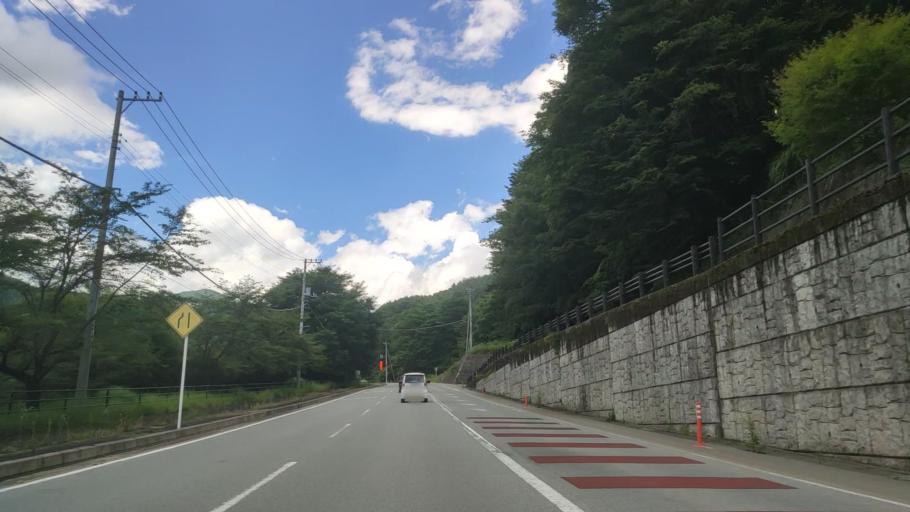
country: JP
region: Yamanashi
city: Enzan
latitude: 35.8034
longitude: 138.7502
